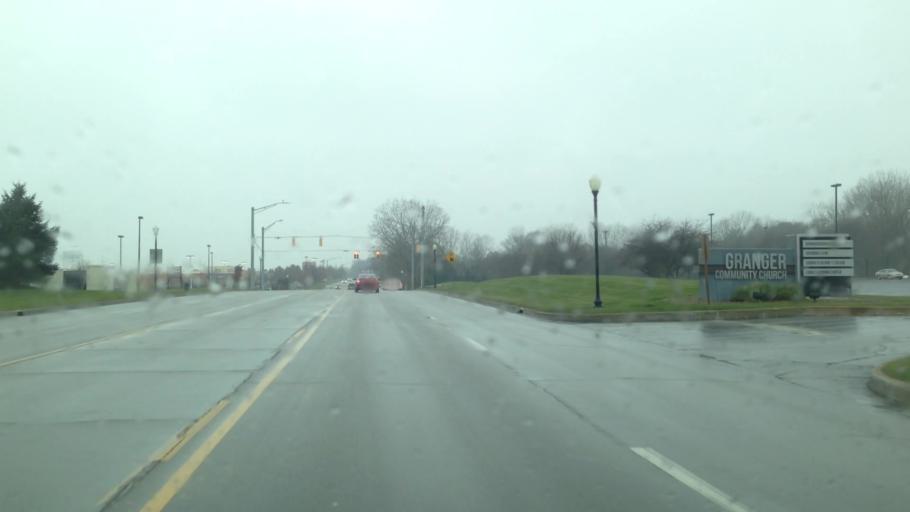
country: US
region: Indiana
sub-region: Saint Joseph County
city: Georgetown
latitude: 41.7205
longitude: -86.1695
